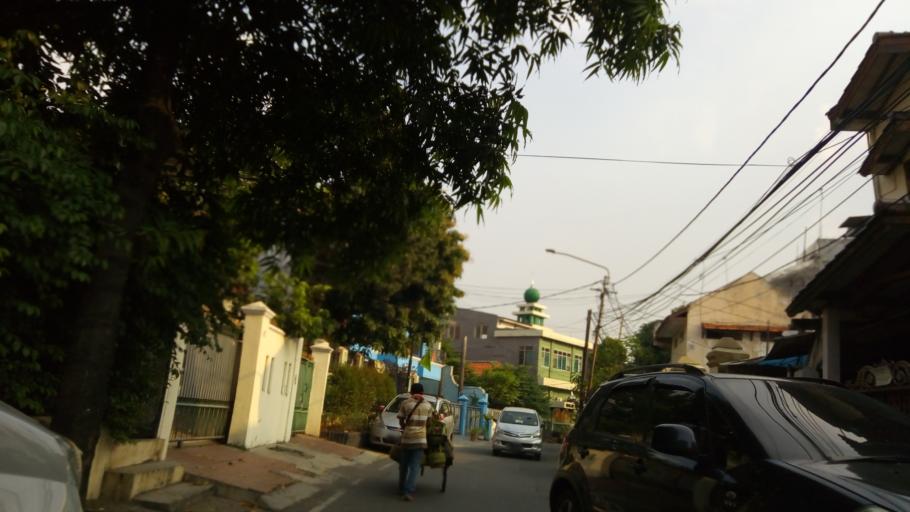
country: ID
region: Jakarta Raya
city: Jakarta
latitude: -6.1943
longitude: 106.8550
